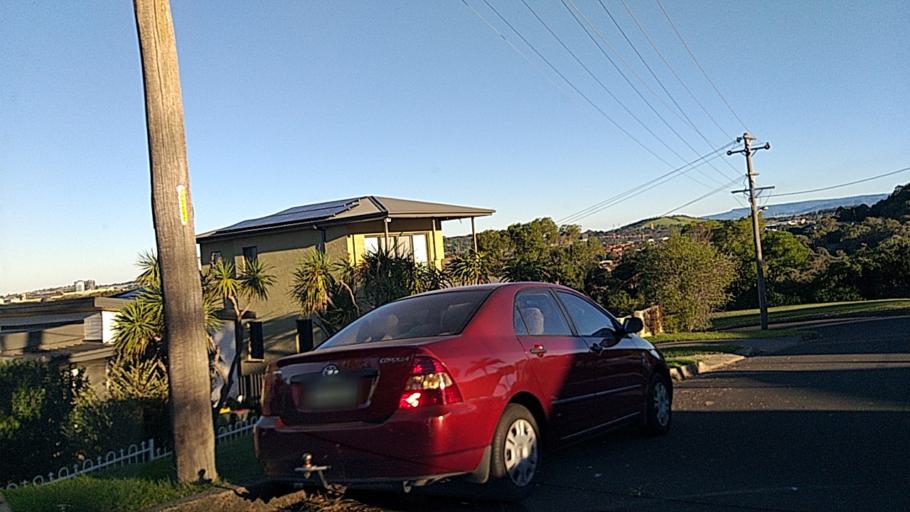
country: AU
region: New South Wales
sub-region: Wollongong
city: West Wollongong
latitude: -34.4366
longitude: 150.8571
